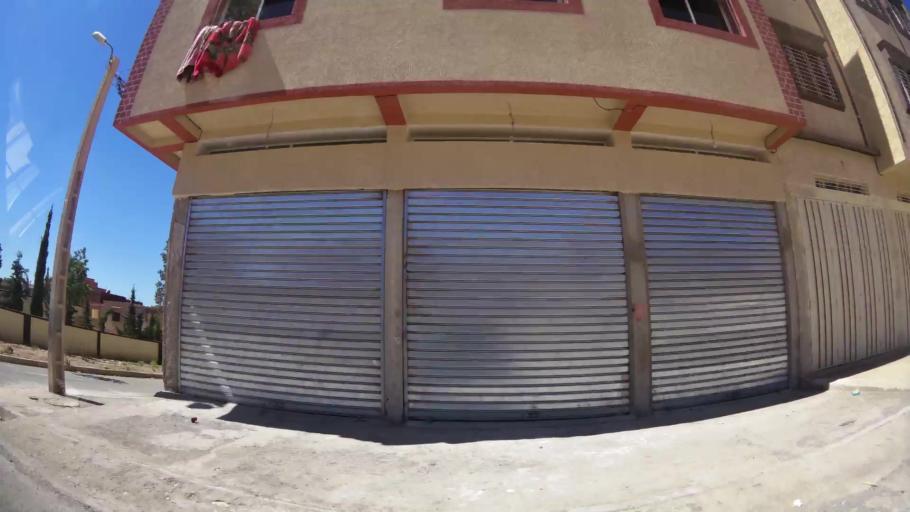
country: MA
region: Oriental
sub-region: Oujda-Angad
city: Oujda
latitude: 34.6601
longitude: -1.8709
